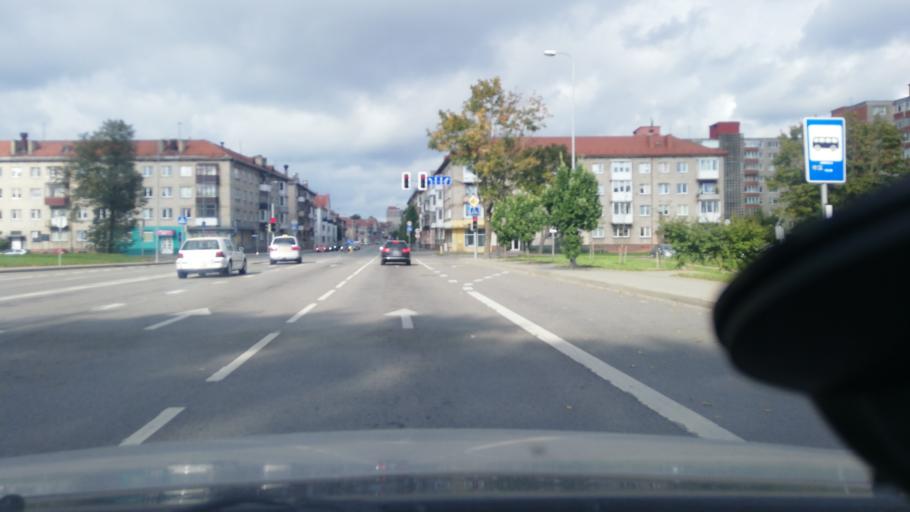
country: LT
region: Klaipedos apskritis
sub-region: Klaipeda
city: Klaipeda
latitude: 55.6752
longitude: 21.1551
